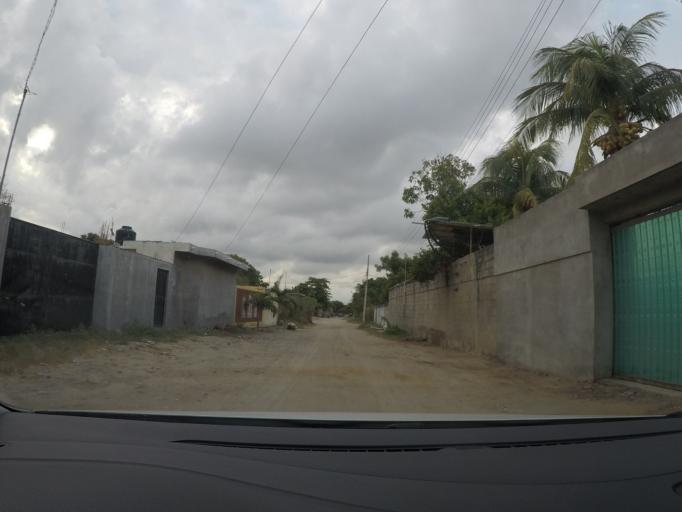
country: MX
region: Oaxaca
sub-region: Salina Cruz
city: Salina Cruz
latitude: 16.2078
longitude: -95.1998
